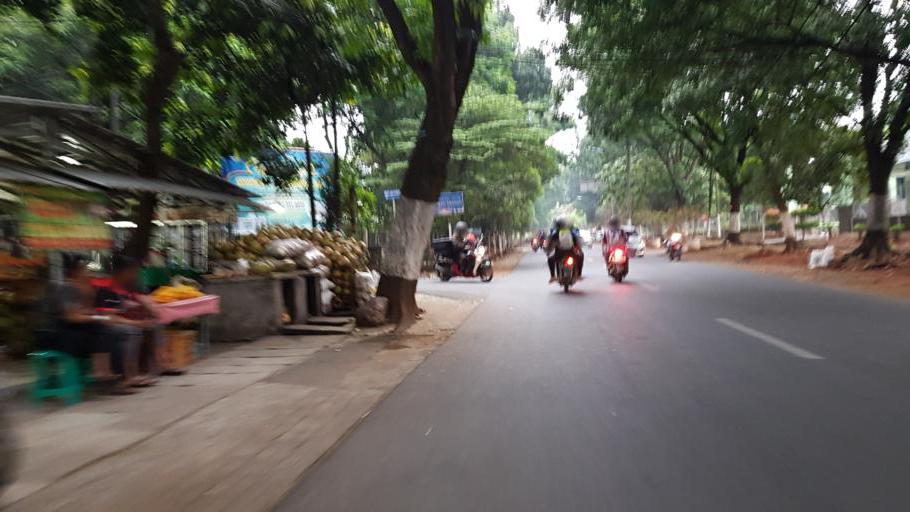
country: ID
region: West Java
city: Depok
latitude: -6.3335
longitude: 106.8458
